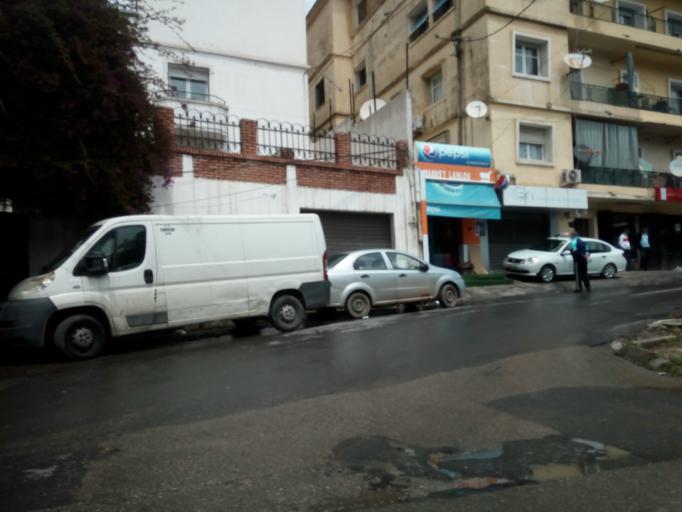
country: DZ
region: Alger
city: Algiers
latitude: 36.7708
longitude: 3.0386
